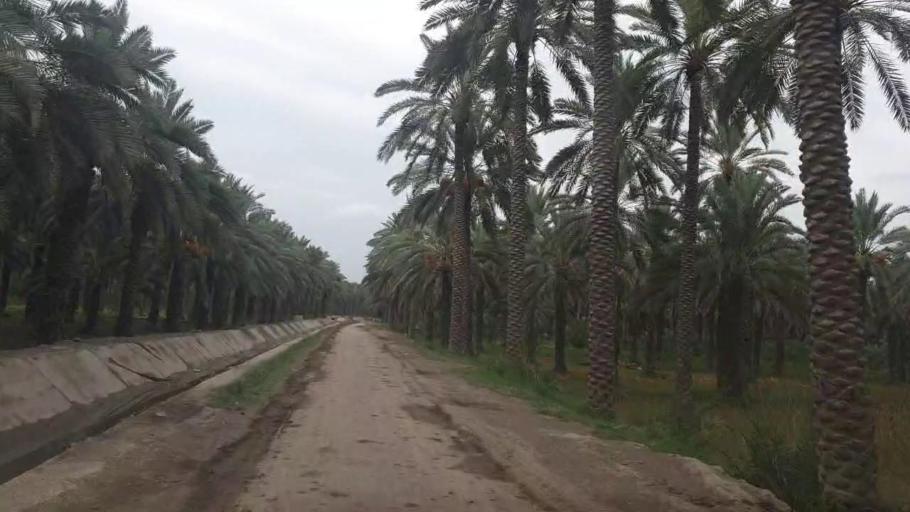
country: PK
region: Sindh
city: Khairpur
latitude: 27.5947
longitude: 68.8005
